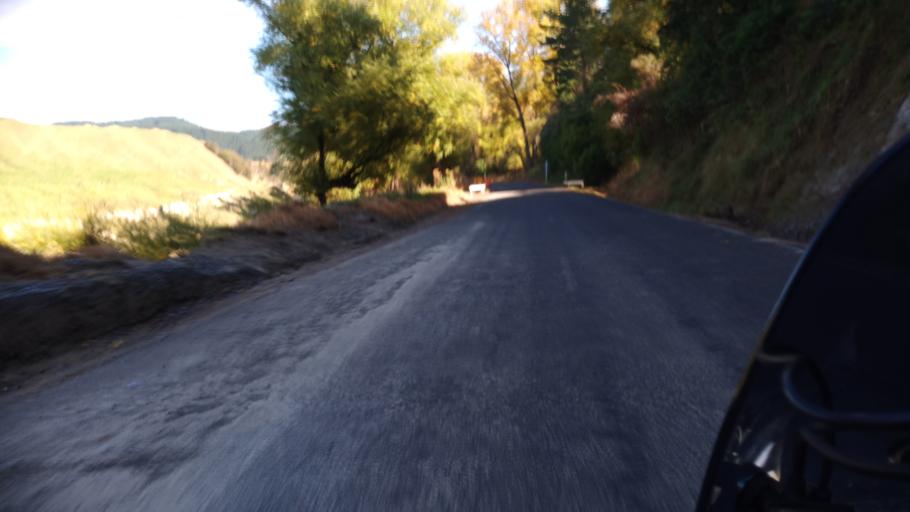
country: NZ
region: Hawke's Bay
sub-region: Wairoa District
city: Wairoa
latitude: -38.9204
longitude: 177.2560
